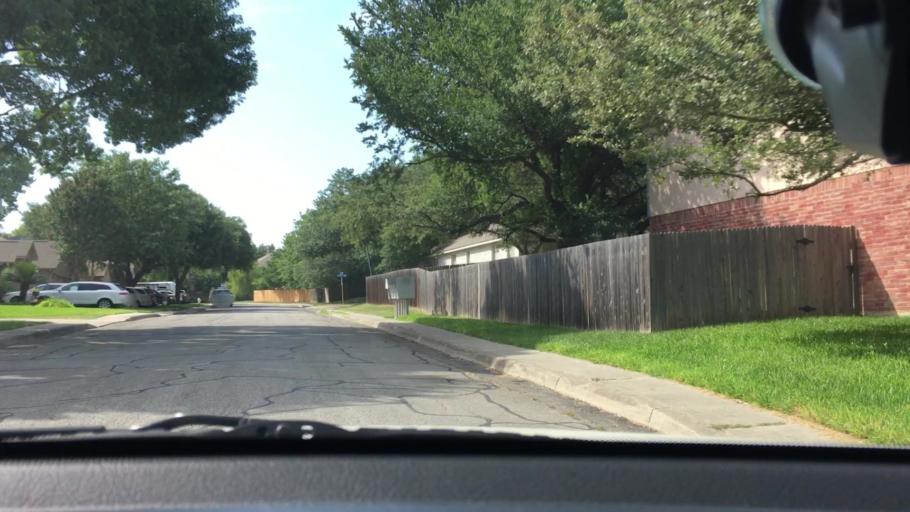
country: US
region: Texas
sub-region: Bexar County
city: Live Oak
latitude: 29.5812
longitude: -98.3801
